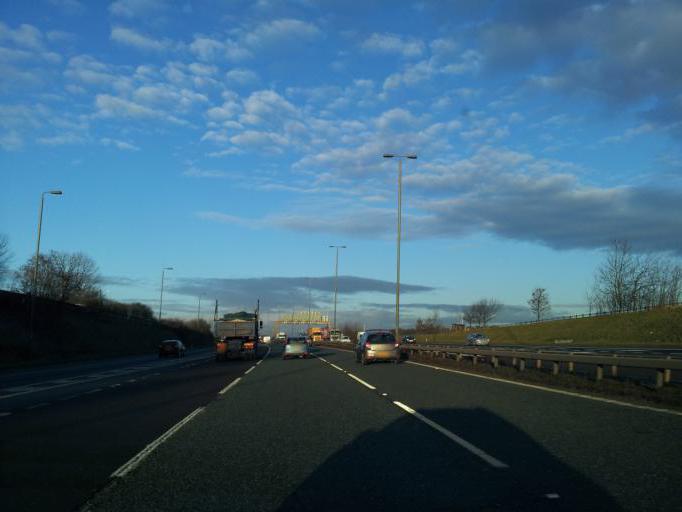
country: GB
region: England
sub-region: City and Borough of Leeds
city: Lofthouse
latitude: 53.7339
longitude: -1.5279
